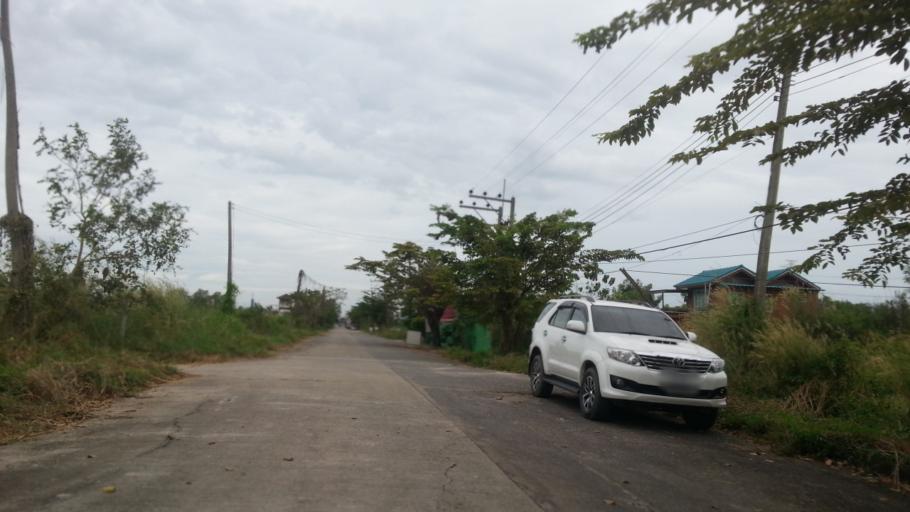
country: TH
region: Pathum Thani
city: Nong Suea
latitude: 14.0653
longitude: 100.8784
